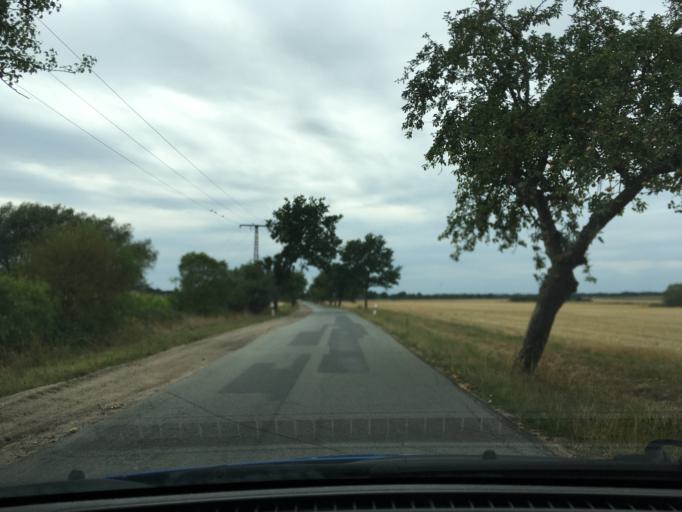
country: DE
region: Mecklenburg-Vorpommern
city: Wittenburg
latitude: 53.5162
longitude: 11.1279
